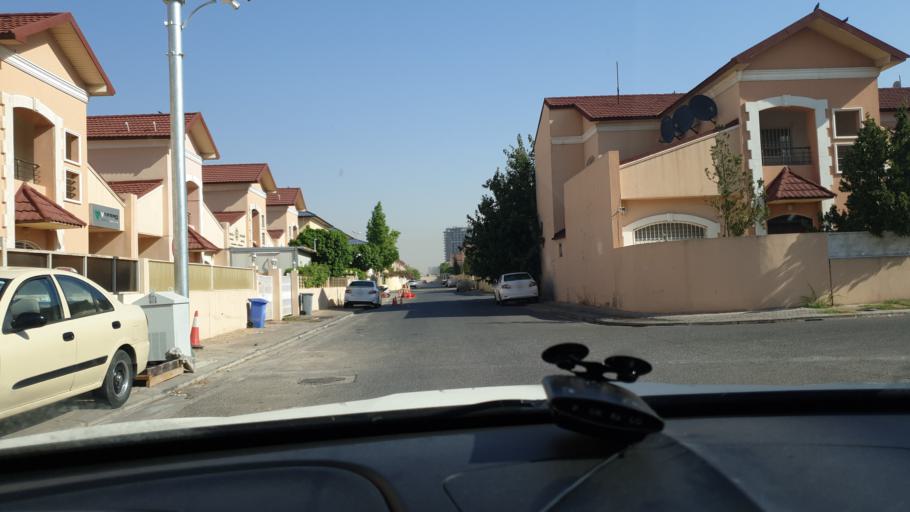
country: IQ
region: Arbil
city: Erbil
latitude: 36.1861
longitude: 43.9653
